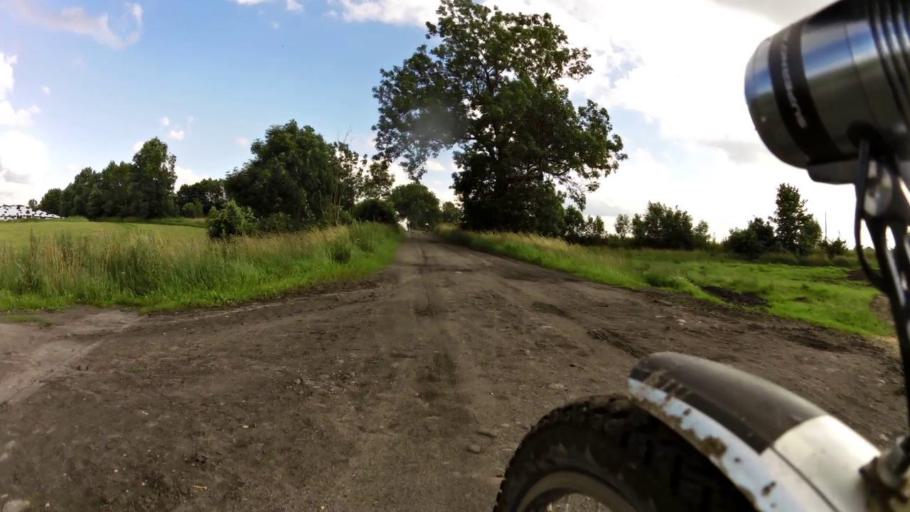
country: PL
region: West Pomeranian Voivodeship
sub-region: Powiat swidwinski
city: Swidwin
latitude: 53.7721
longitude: 15.8612
